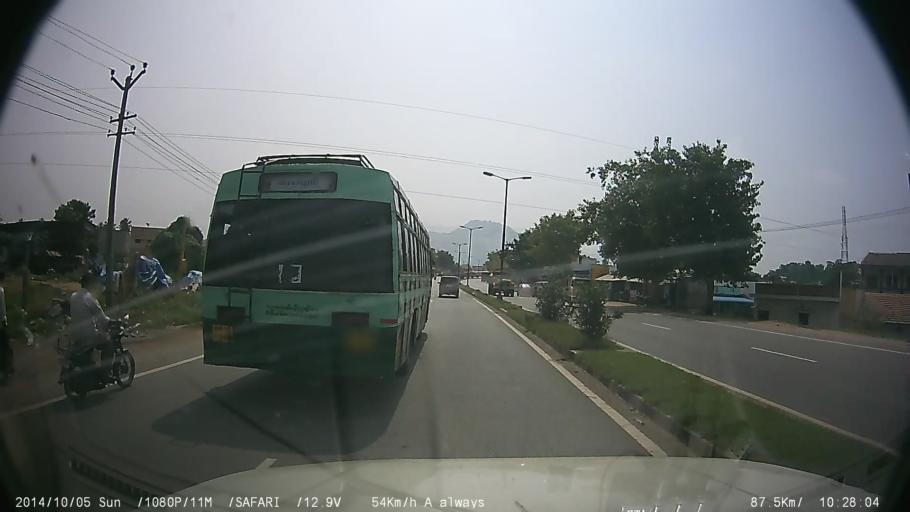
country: IN
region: Tamil Nadu
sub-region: Salem
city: Salem
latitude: 11.6305
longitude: 78.1301
